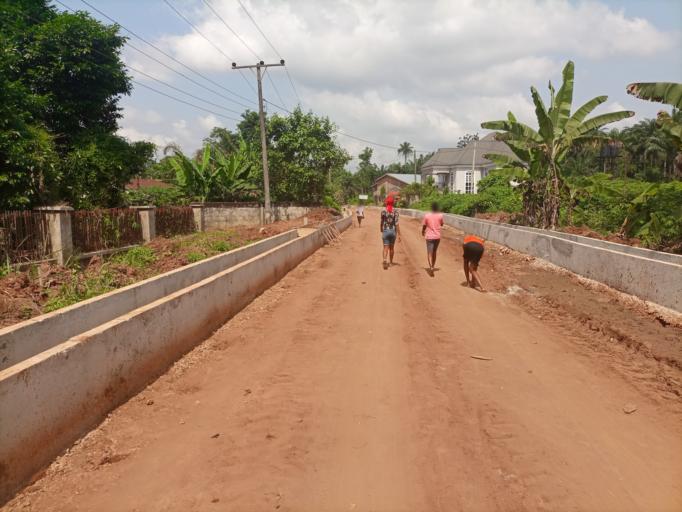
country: NG
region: Imo
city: Ihuo
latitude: 5.5269
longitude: 7.2622
